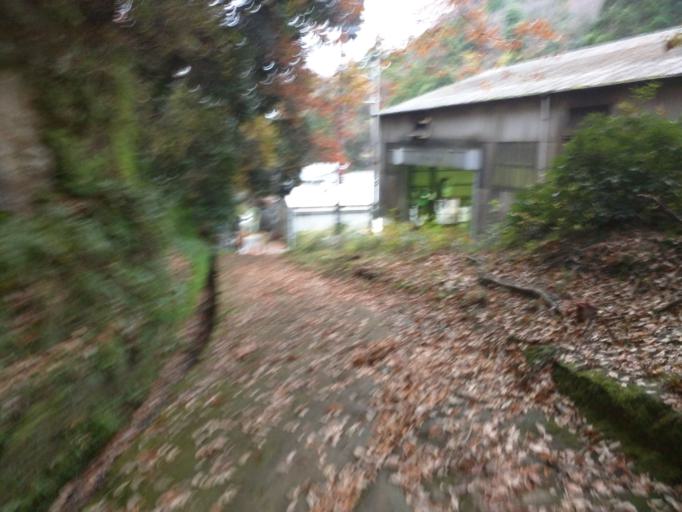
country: JP
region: Kanagawa
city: Zushi
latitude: 35.3286
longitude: 139.5950
